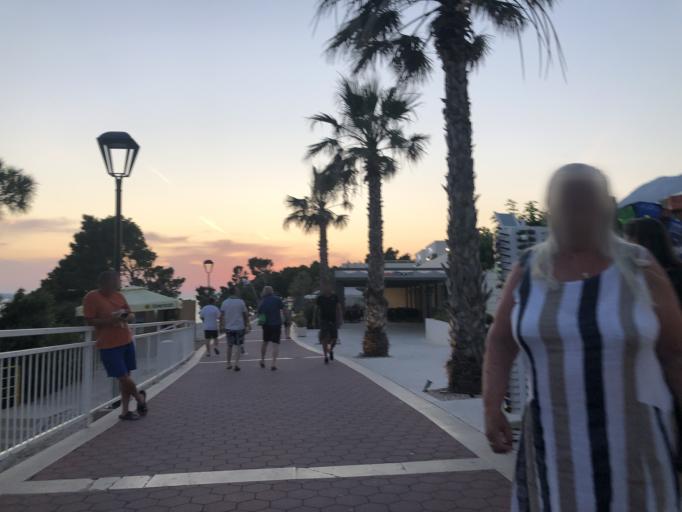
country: HR
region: Splitsko-Dalmatinska
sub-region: Grad Makarska
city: Makarska
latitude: 43.3062
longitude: 17.0024
